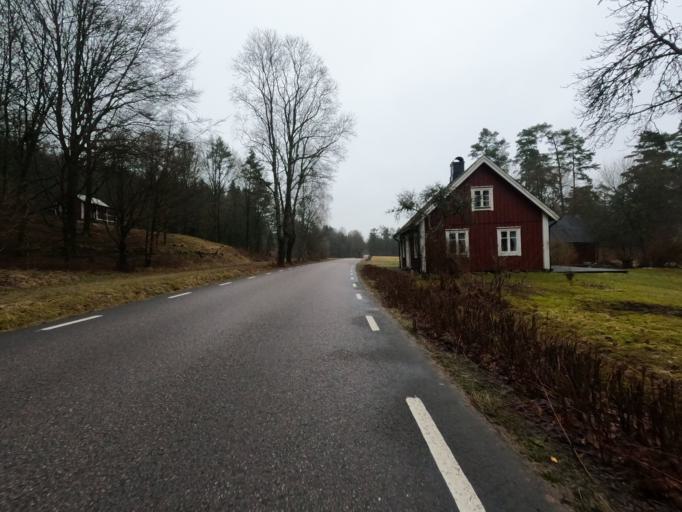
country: SE
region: Halland
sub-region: Halmstads Kommun
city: Oskarstrom
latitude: 56.7606
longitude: 13.1720
